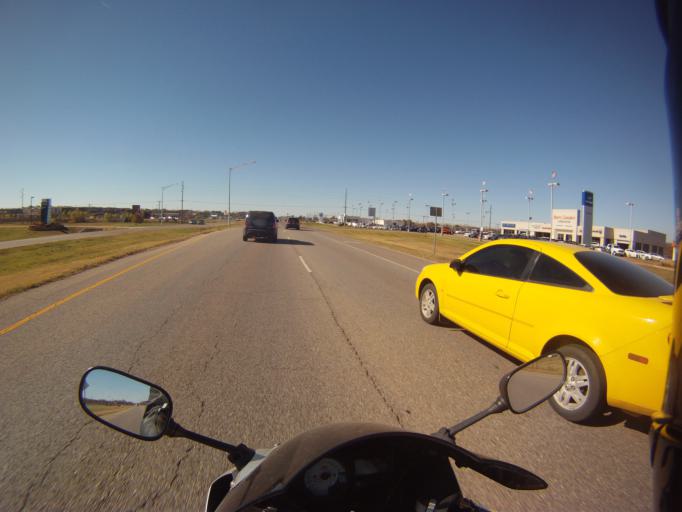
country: US
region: Oklahoma
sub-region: Payne County
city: Stillwater
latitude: 36.1160
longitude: -97.1120
